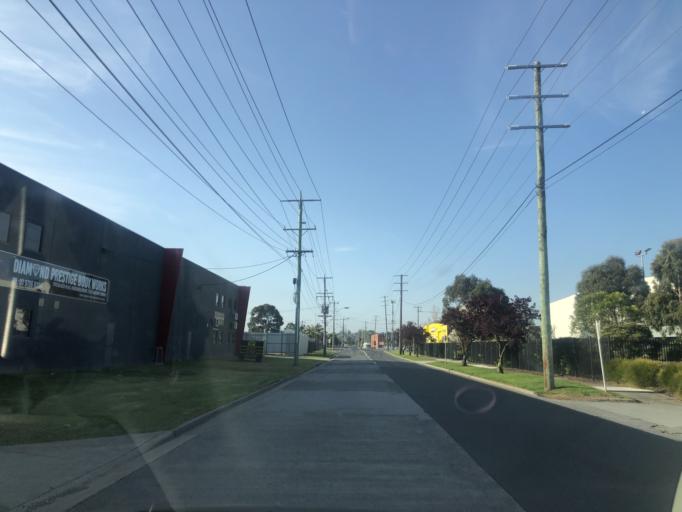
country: AU
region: Victoria
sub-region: Casey
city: Doveton
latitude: -38.0038
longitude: 145.2363
